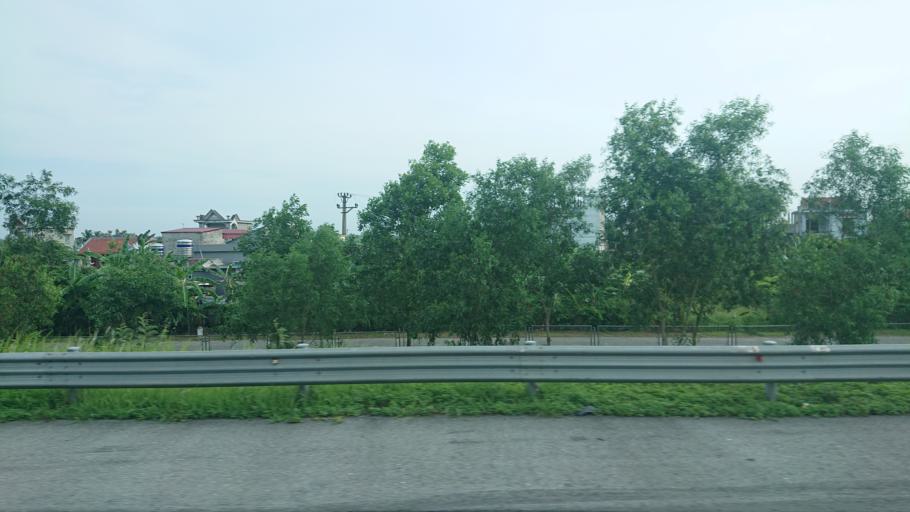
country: VN
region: Hai Phong
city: An Lao
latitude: 20.8129
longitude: 106.4995
